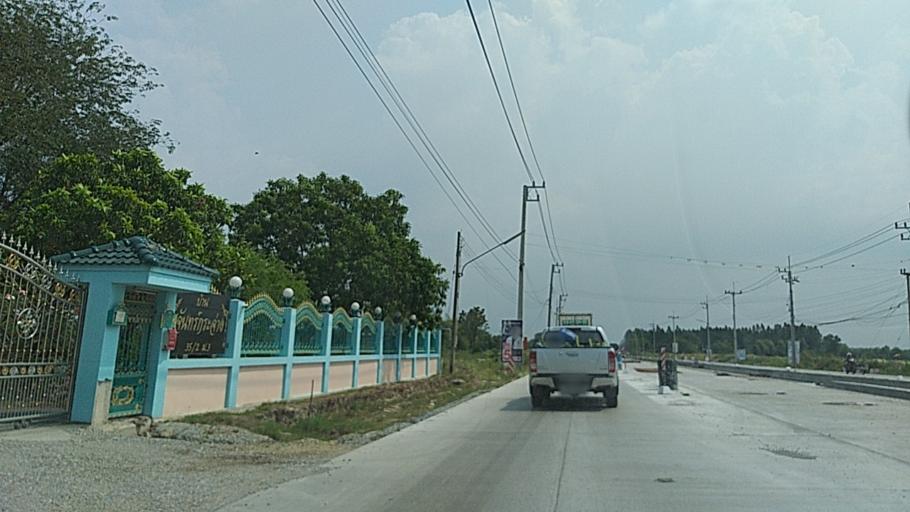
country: TH
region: Chon Buri
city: Phanat Nikhom
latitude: 13.3804
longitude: 101.1940
